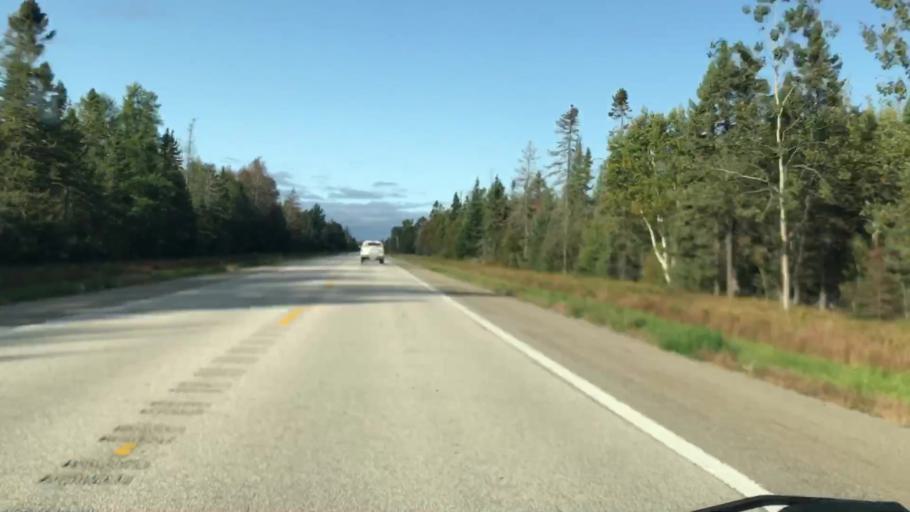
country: US
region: Michigan
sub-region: Luce County
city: Newberry
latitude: 46.3253
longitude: -85.1696
